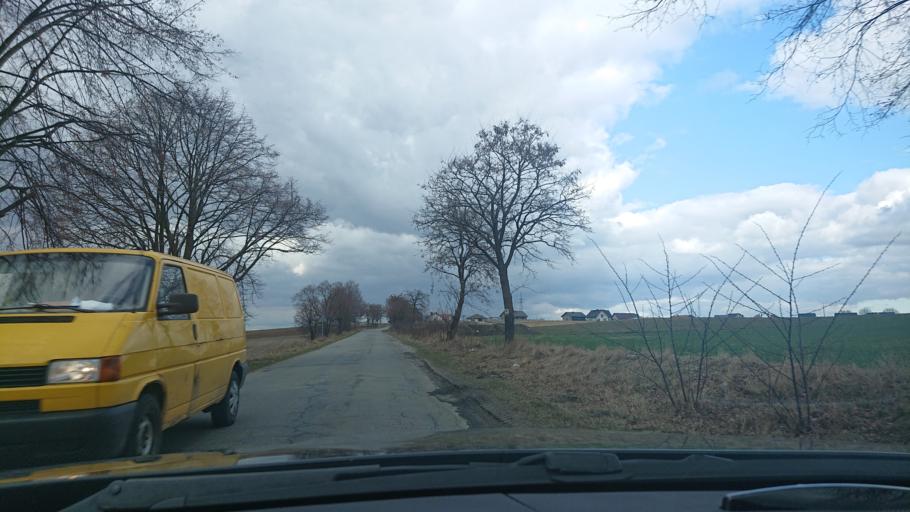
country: PL
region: Greater Poland Voivodeship
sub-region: Powiat gnieznienski
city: Niechanowo
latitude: 52.5574
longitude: 17.6970
